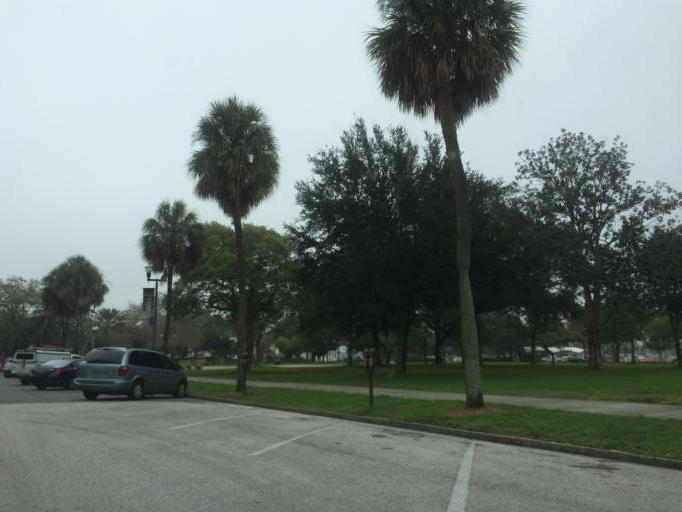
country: US
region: Florida
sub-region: Pinellas County
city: Saint Petersburg
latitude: 27.7725
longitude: -82.6331
